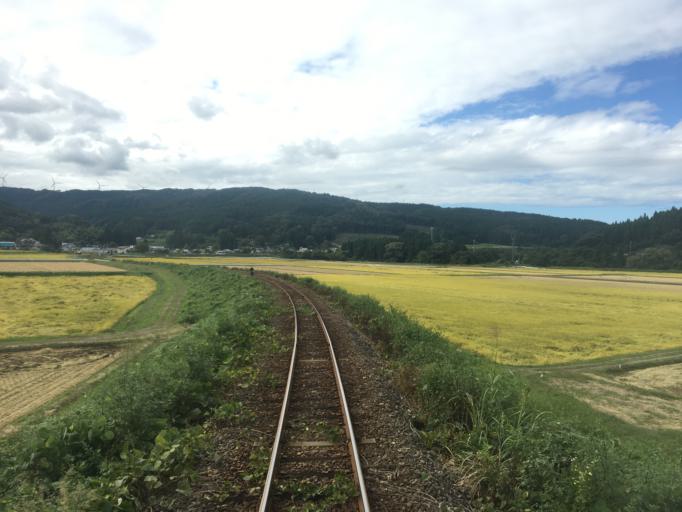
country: JP
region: Yamagata
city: Yuza
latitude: 39.2476
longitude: 140.1277
